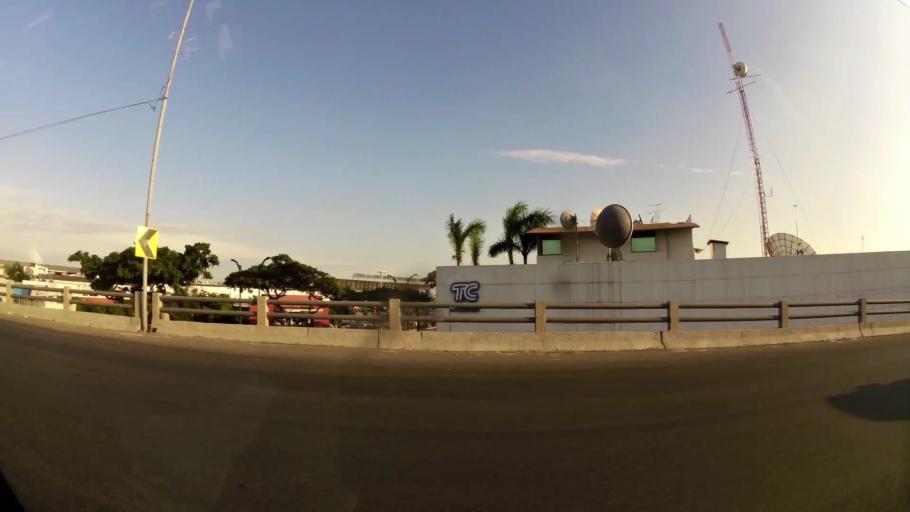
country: EC
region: Guayas
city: Eloy Alfaro
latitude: -2.1569
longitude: -79.8878
